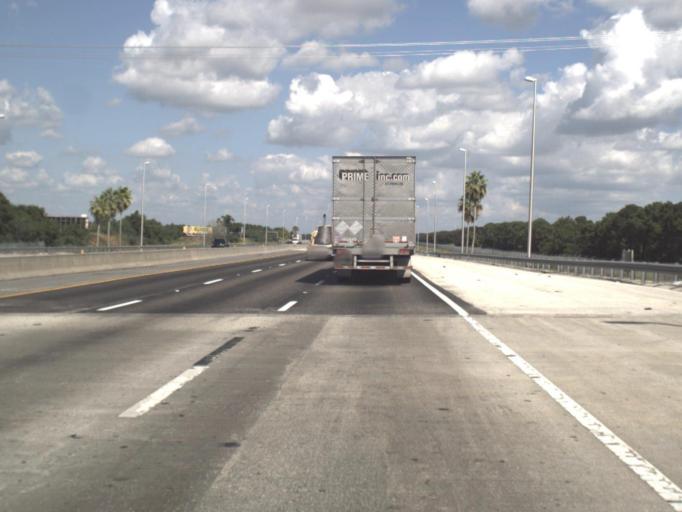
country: US
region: Florida
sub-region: Palm Beach County
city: Villages of Oriole
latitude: 26.4837
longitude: -80.1724
